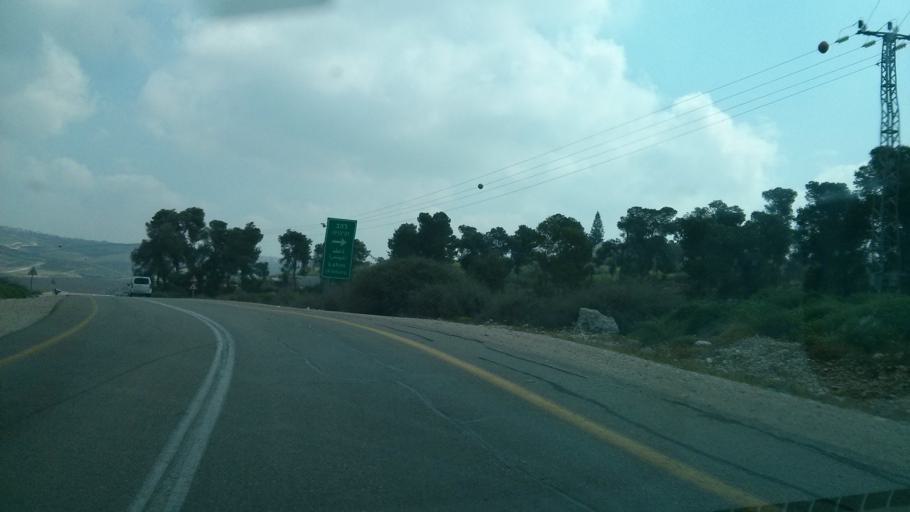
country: PS
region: West Bank
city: Ar Ramadin
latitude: 31.3838
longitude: 34.8674
